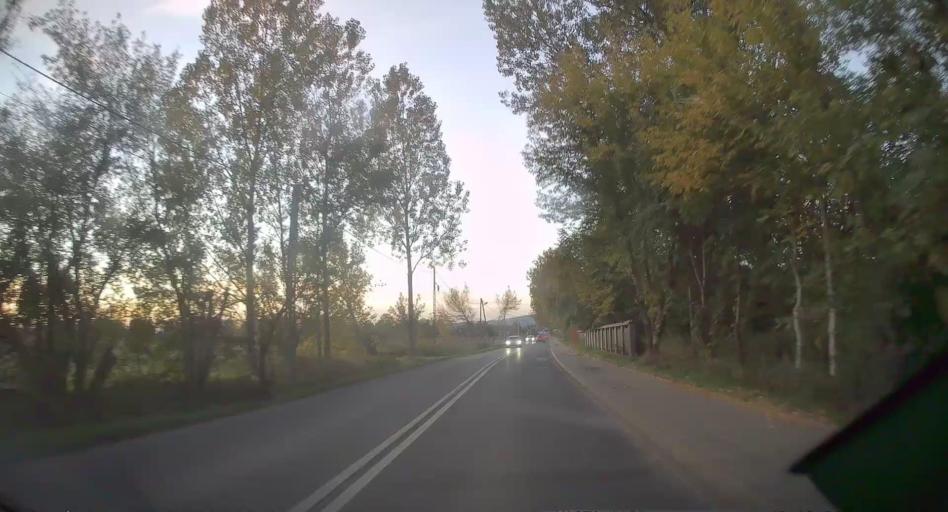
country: PL
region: Lesser Poland Voivodeship
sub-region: Powiat krakowski
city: Rzaska
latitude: 50.1186
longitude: 19.8263
